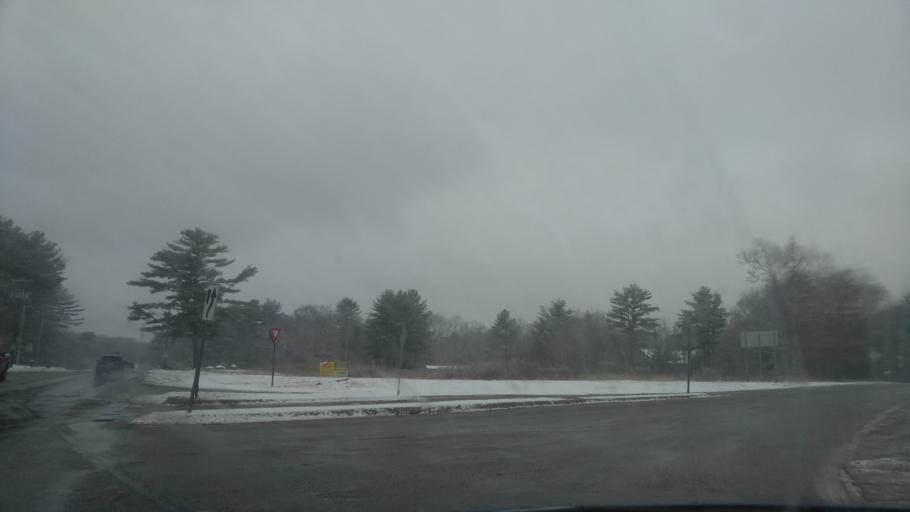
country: US
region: Rhode Island
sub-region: Providence County
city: Foster
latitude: 41.8151
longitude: -71.7338
